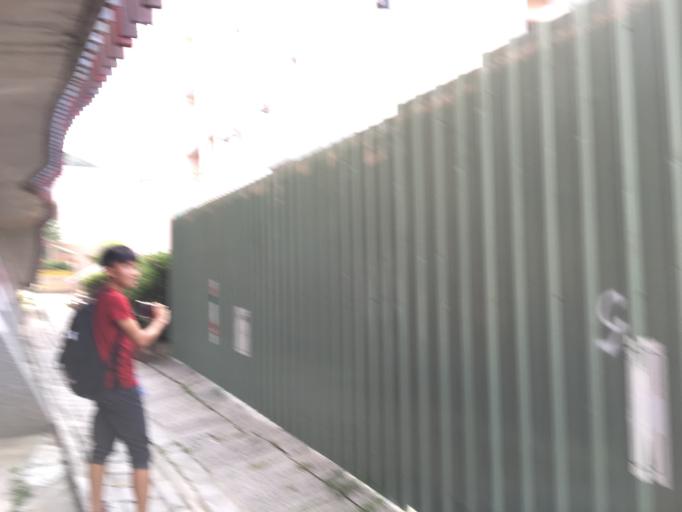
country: TW
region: Taiwan
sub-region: Changhua
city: Chang-hua
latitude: 24.0815
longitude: 120.5596
